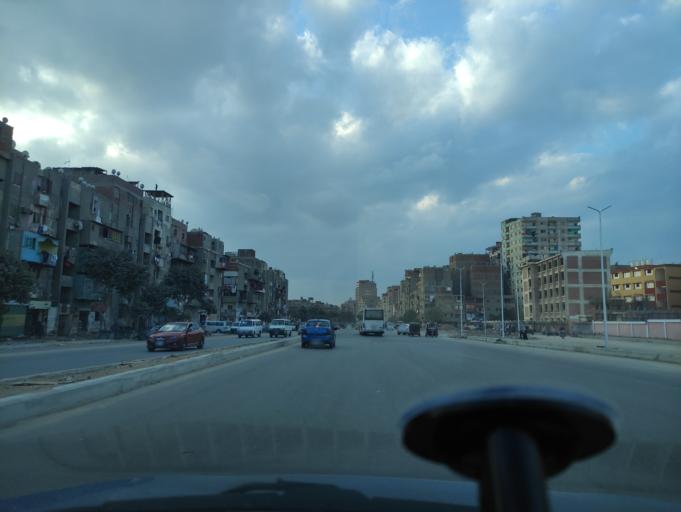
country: EG
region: Muhafazat al Qalyubiyah
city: Al Khankah
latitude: 30.1360
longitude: 31.3526
